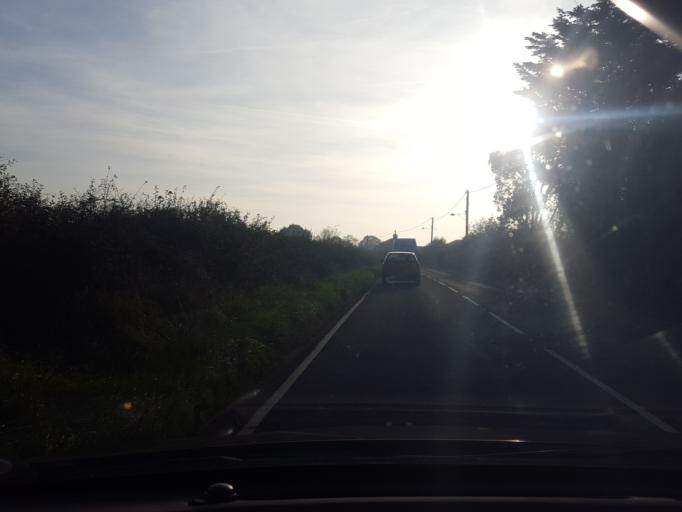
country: GB
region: England
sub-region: Essex
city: Frinton-on-Sea
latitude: 51.8348
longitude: 1.2119
